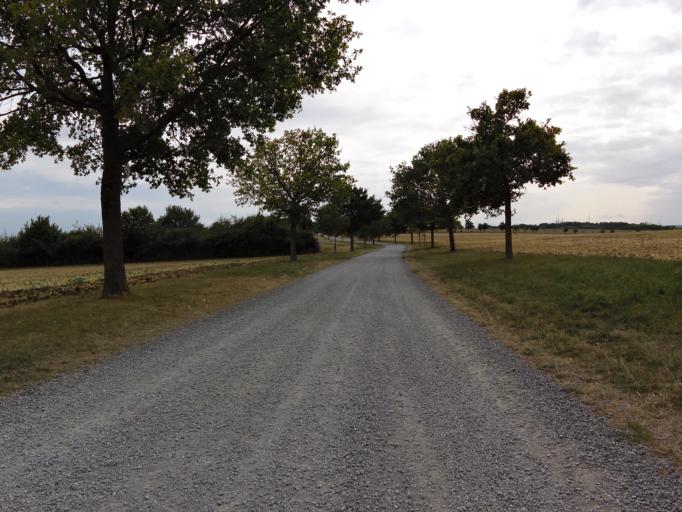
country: DE
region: Bavaria
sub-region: Regierungsbezirk Unterfranken
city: Wuerzburg
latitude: 49.8178
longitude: 9.9396
